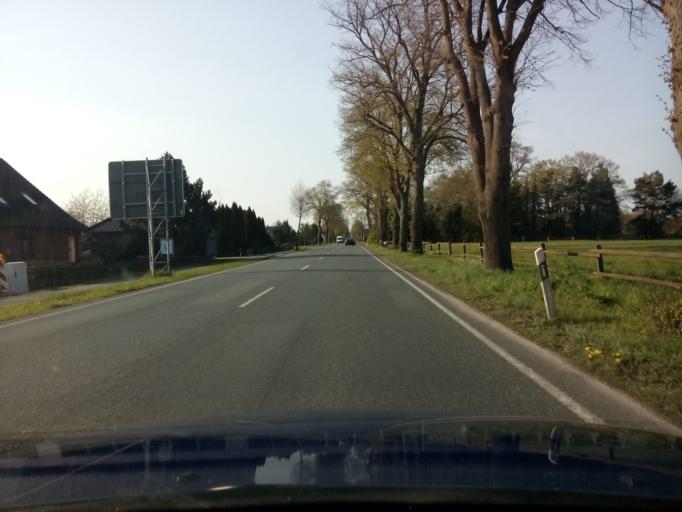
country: DE
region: Lower Saxony
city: Syke
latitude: 52.9648
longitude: 8.7979
